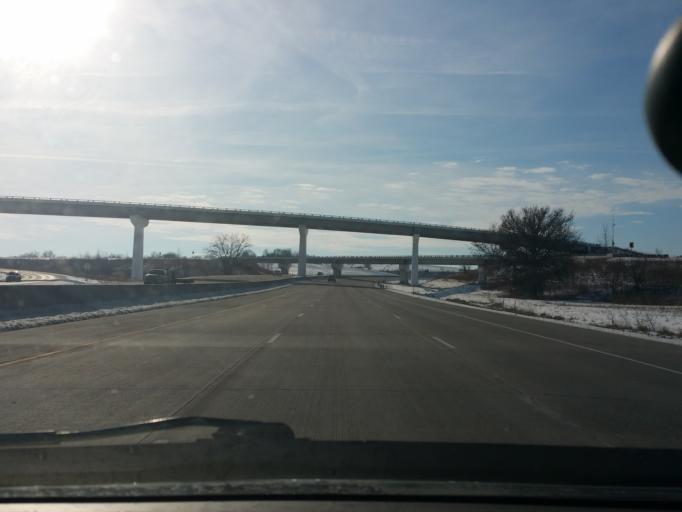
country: US
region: Iowa
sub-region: Polk County
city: West Des Moines
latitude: 41.5266
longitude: -93.7733
